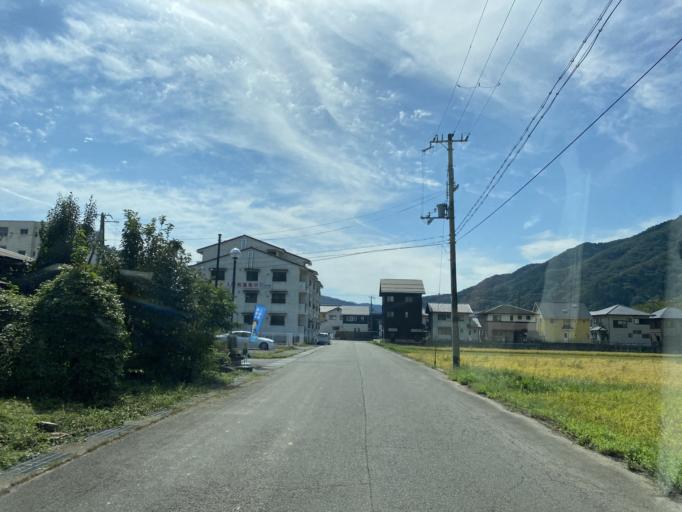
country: JP
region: Hyogo
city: Toyooka
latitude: 35.4347
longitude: 134.7928
